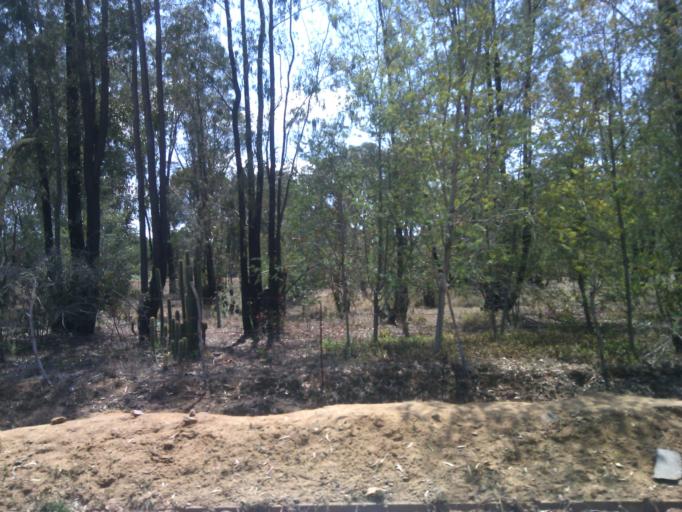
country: ZA
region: Orange Free State
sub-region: Xhariep District Municipality
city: Dewetsdorp
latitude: -29.5781
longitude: 26.6640
